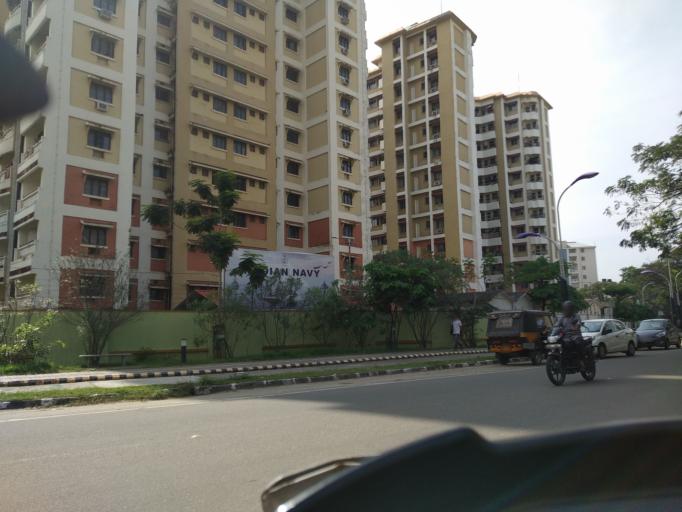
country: IN
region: Kerala
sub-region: Ernakulam
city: Cochin
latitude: 9.9550
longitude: 76.2983
